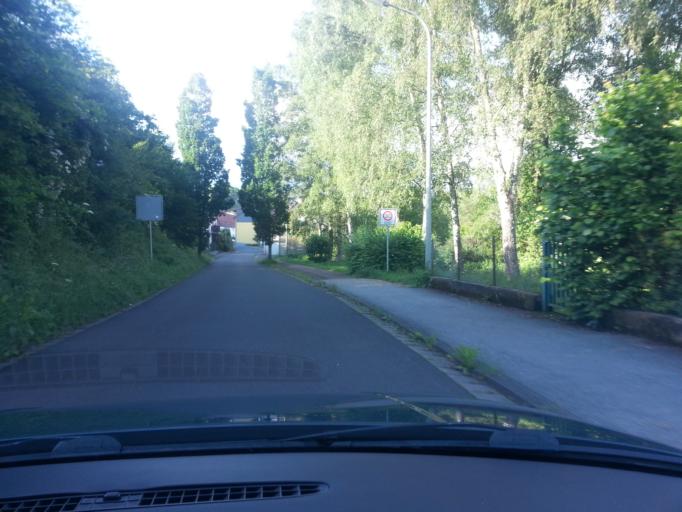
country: DE
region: Rheinland-Pfalz
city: Breitenbach
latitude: 49.4717
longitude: 7.2537
